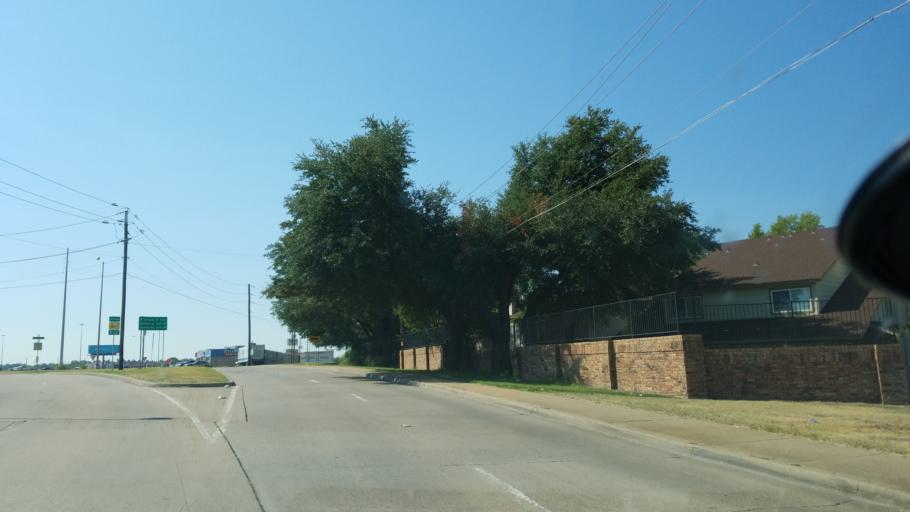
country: US
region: Texas
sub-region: Dallas County
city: Richardson
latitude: 32.9044
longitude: -96.7178
